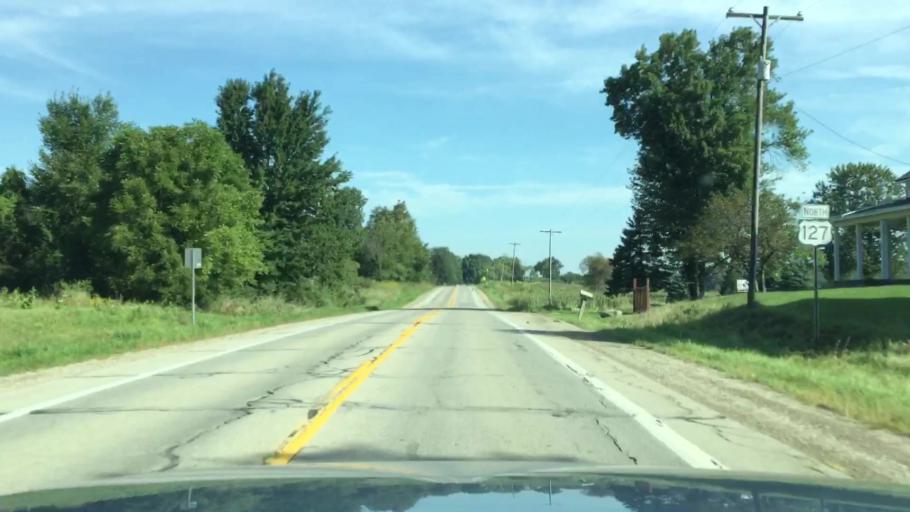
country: US
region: Michigan
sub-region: Lenawee County
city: Manitou Beach-Devils Lake
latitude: 41.9572
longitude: -84.3671
